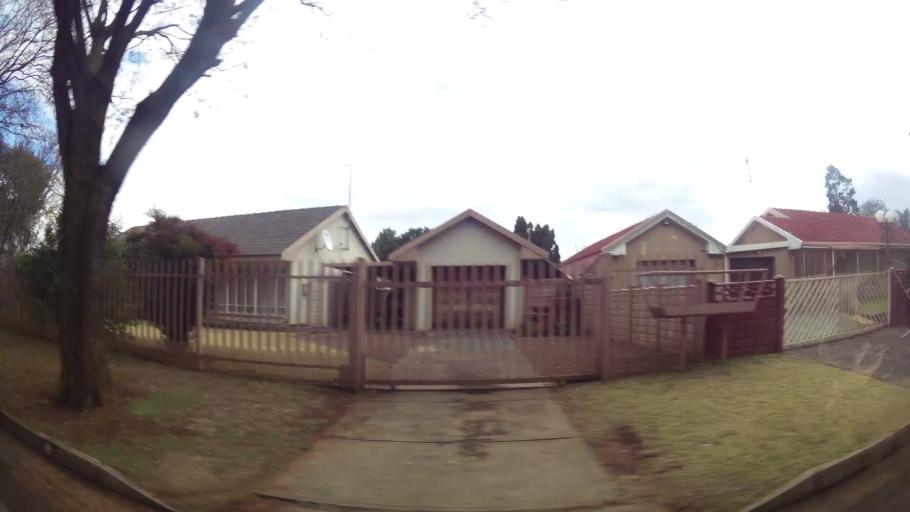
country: ZA
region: Gauteng
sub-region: Sedibeng District Municipality
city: Vereeniging
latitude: -26.6432
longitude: 27.9765
